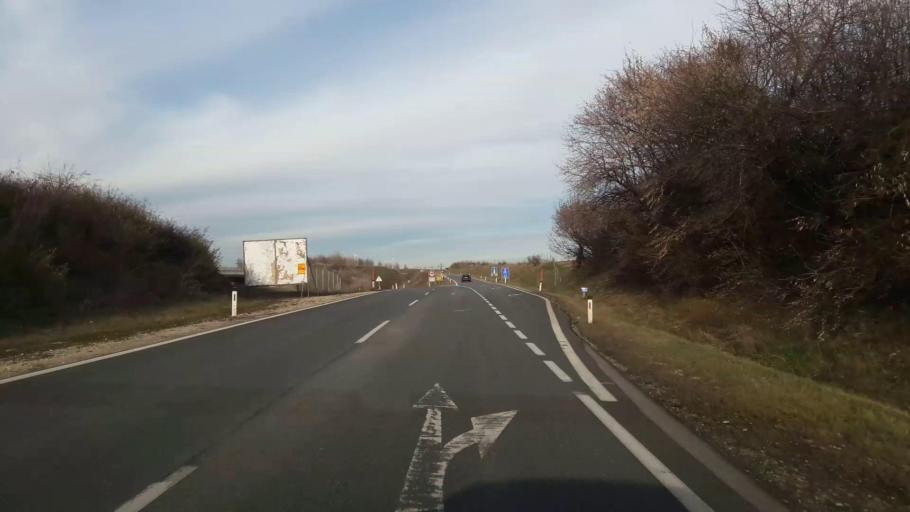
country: AT
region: Lower Austria
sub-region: Politischer Bezirk Mistelbach
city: Gaweinstal
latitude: 48.4922
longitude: 16.5971
